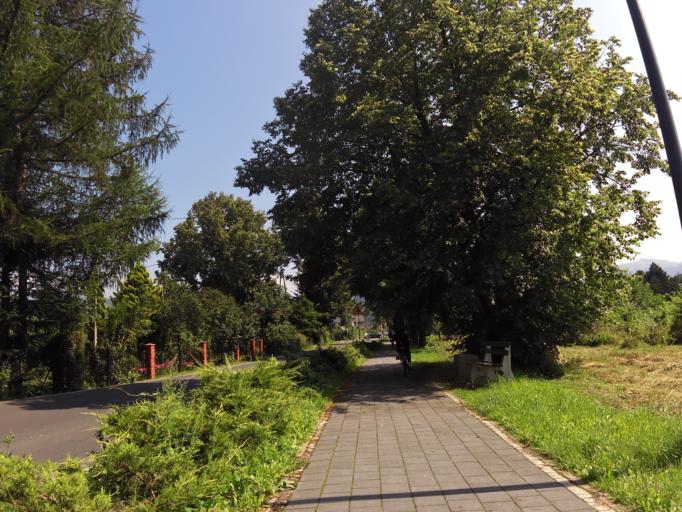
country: PL
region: Silesian Voivodeship
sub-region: Powiat zywiecki
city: Wegierska Gorka
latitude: 49.6151
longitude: 19.1287
